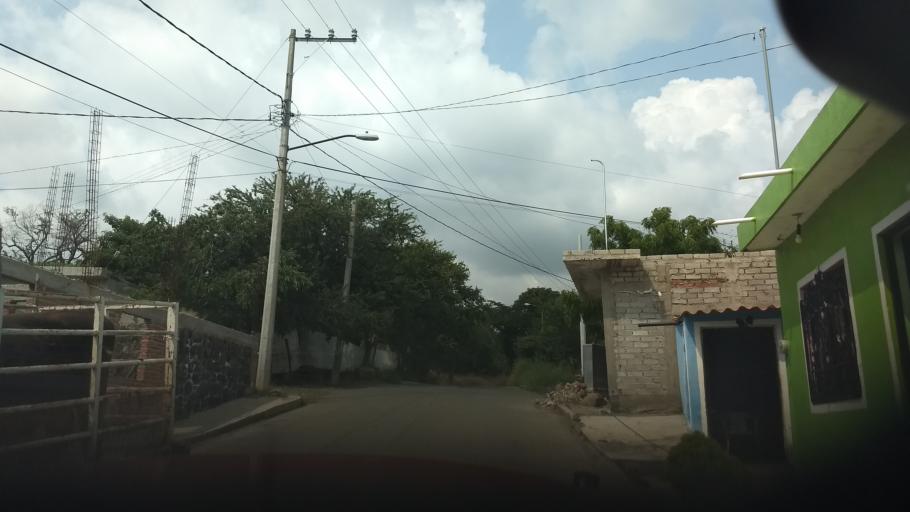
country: MX
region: Jalisco
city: Tonila
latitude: 19.3932
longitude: -103.5285
